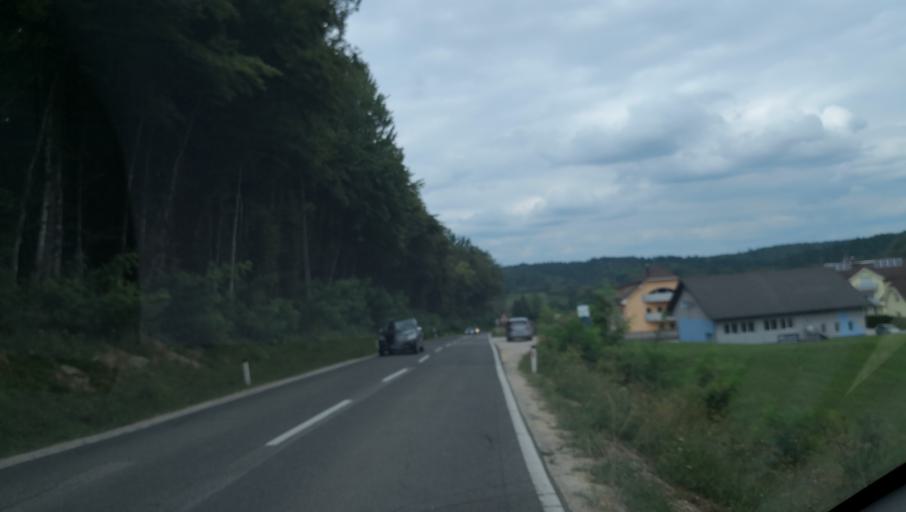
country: SI
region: Novo Mesto
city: Novo Mesto
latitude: 45.7723
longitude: 15.1872
